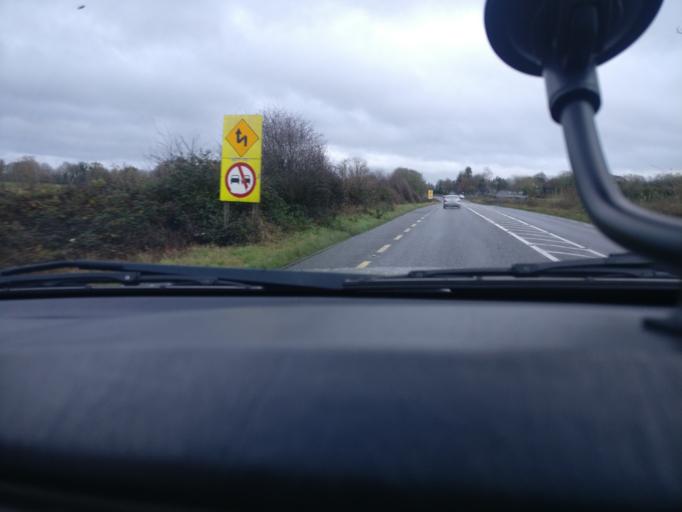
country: IE
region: Leinster
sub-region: An Mhi
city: Enfield
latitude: 53.4177
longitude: -6.7765
